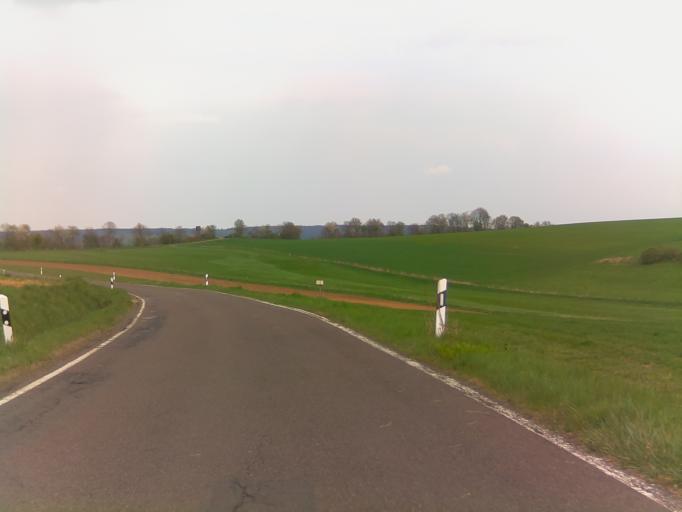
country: DE
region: Rheinland-Pfalz
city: Daubach
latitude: 49.8531
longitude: 7.6234
